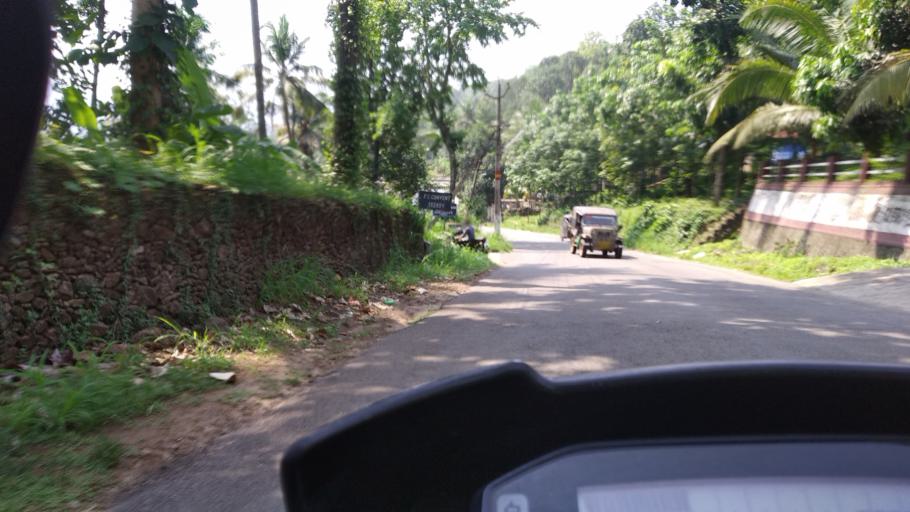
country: IN
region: Kerala
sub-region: Kottayam
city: Erattupetta
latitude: 9.7001
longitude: 76.8068
